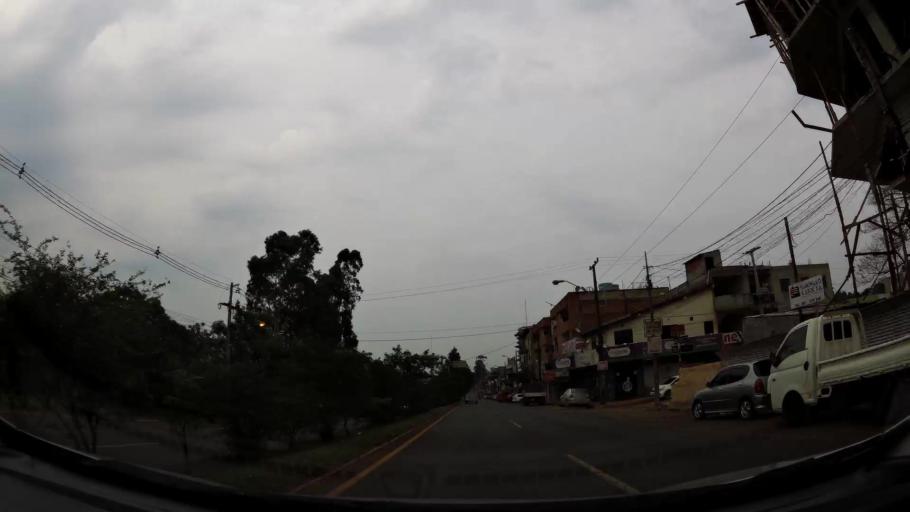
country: PY
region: Alto Parana
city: Ciudad del Este
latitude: -25.5126
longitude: -54.6410
